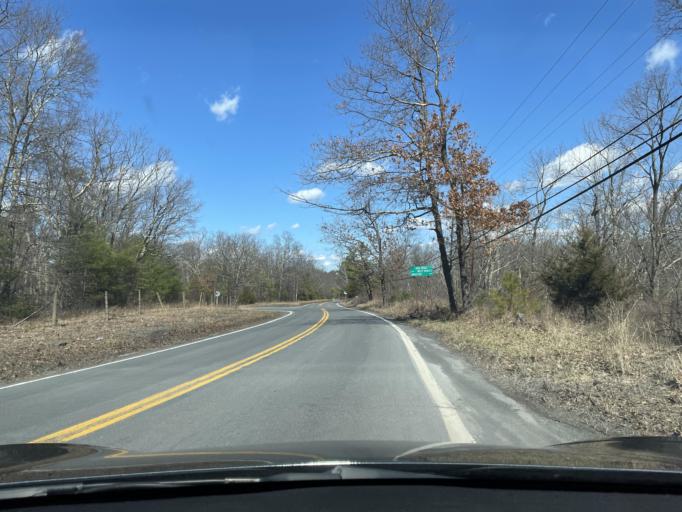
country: US
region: New York
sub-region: Ulster County
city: West Hurley
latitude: 41.9732
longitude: -74.1029
